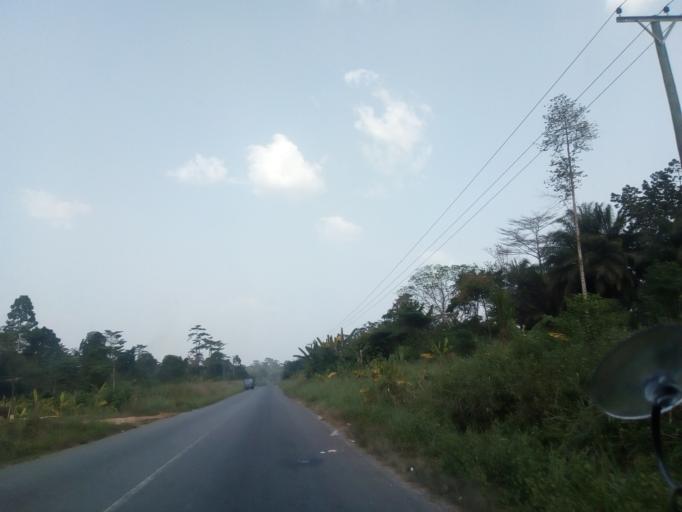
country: GH
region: Eastern
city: Suhum
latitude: 6.0490
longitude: -0.4099
